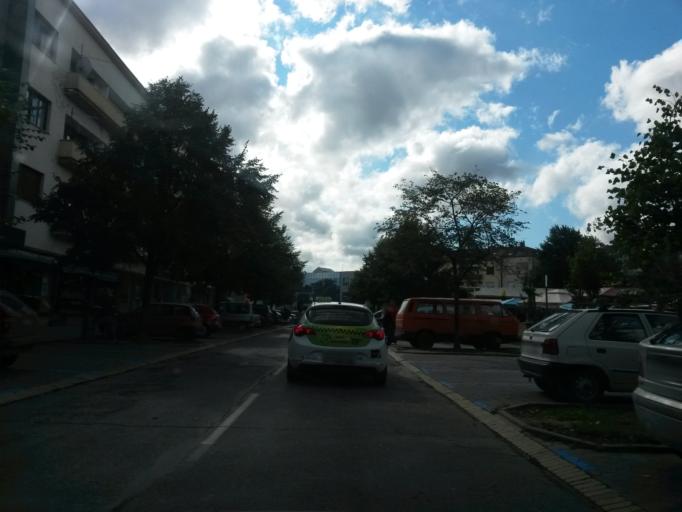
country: HR
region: Osjecko-Baranjska
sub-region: Grad Osijek
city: Osijek
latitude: 45.5560
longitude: 18.7197
